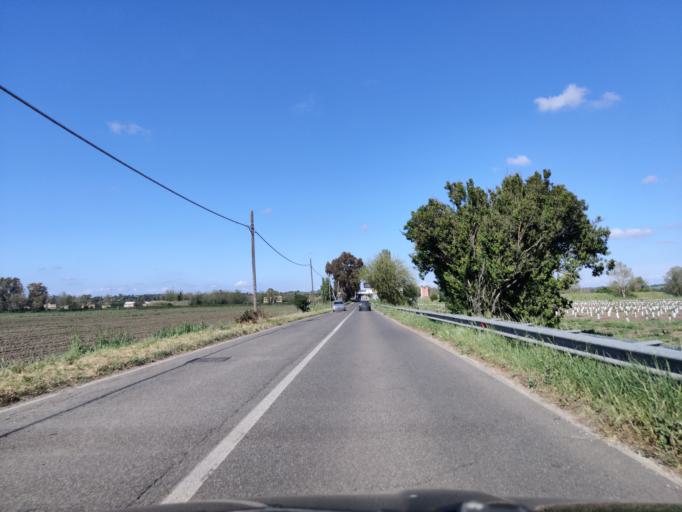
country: IT
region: Latium
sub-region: Citta metropolitana di Roma Capitale
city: Maccarese
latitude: 41.8838
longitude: 12.2206
